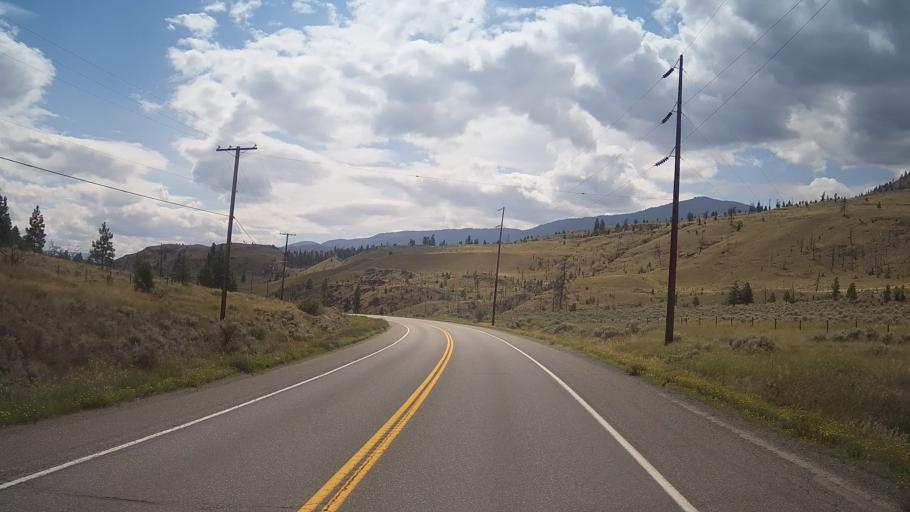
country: CA
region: British Columbia
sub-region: Thompson-Nicola Regional District
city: Ashcroft
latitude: 50.6341
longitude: -121.3466
